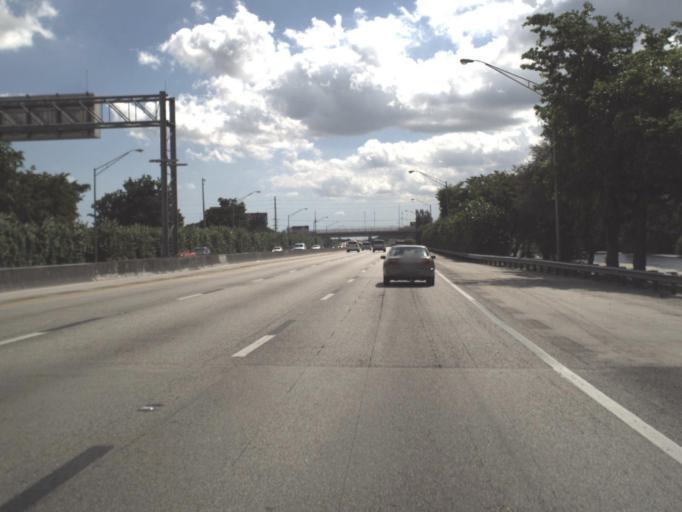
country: US
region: Florida
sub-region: Broward County
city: Davie
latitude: 26.0506
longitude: -80.2150
